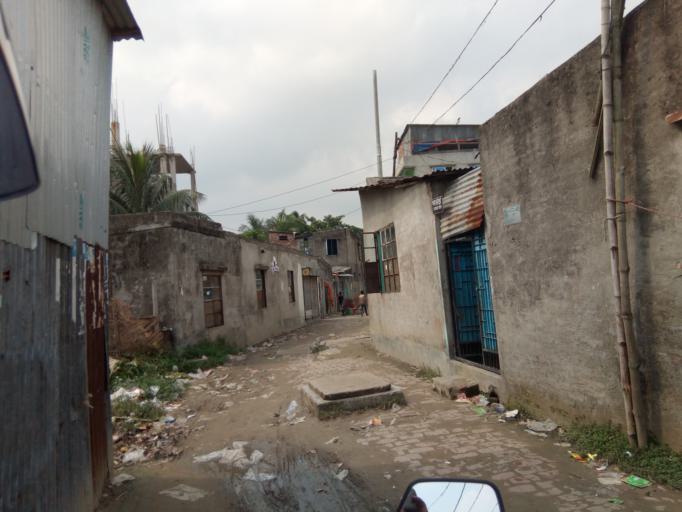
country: BD
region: Dhaka
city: Paltan
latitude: 23.7463
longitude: 90.4478
